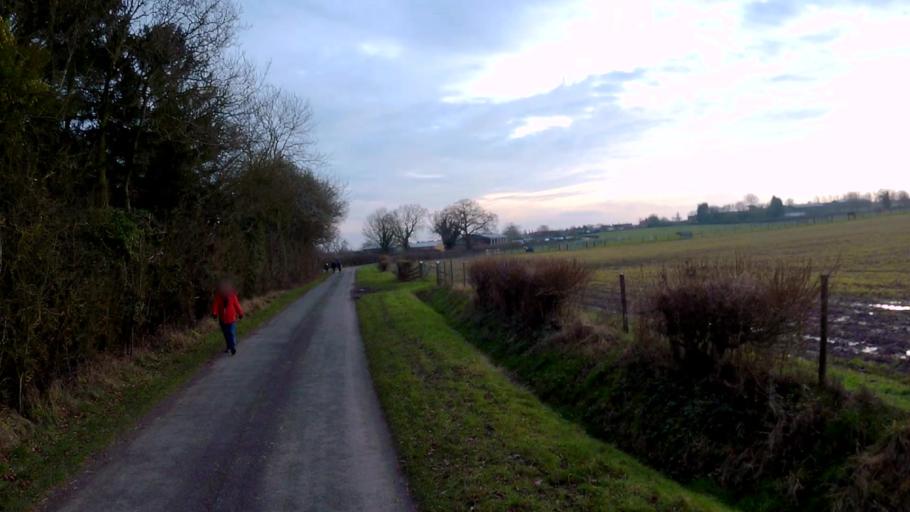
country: GB
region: England
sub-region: Lincolnshire
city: Bourne
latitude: 52.8173
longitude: -0.3993
